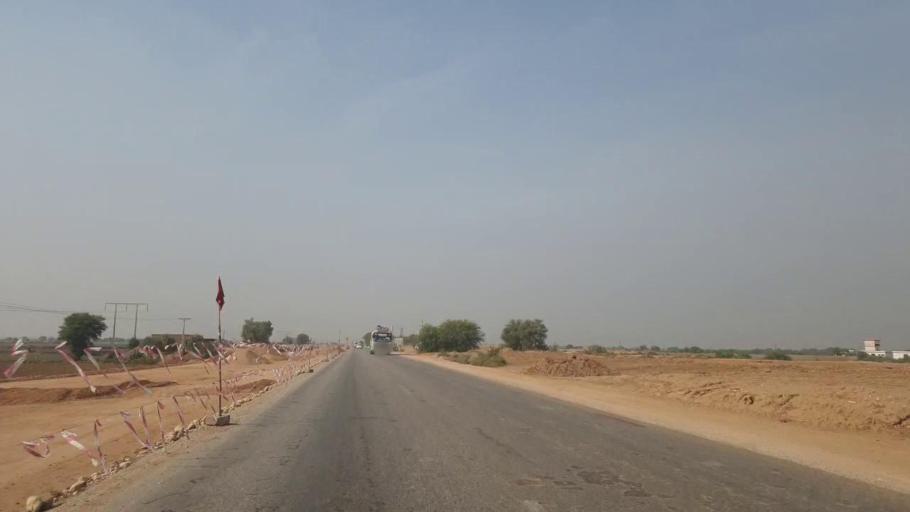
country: PK
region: Sindh
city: Sann
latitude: 26.1314
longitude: 68.0484
